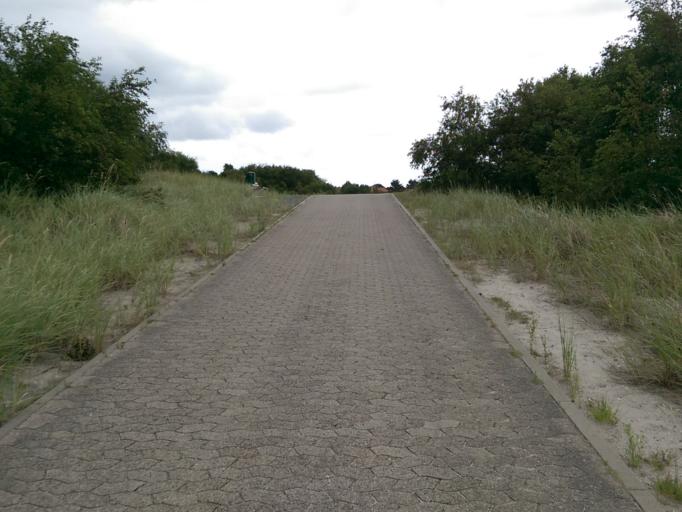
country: DE
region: Lower Saxony
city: Spiekeroog
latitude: 53.7682
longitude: 7.7215
